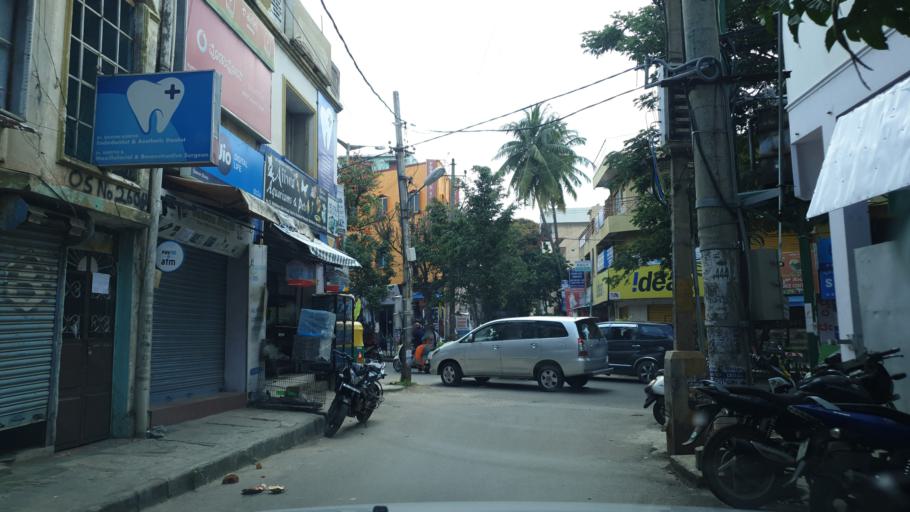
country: IN
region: Karnataka
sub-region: Bangalore Urban
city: Bangalore
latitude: 13.0302
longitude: 77.5608
